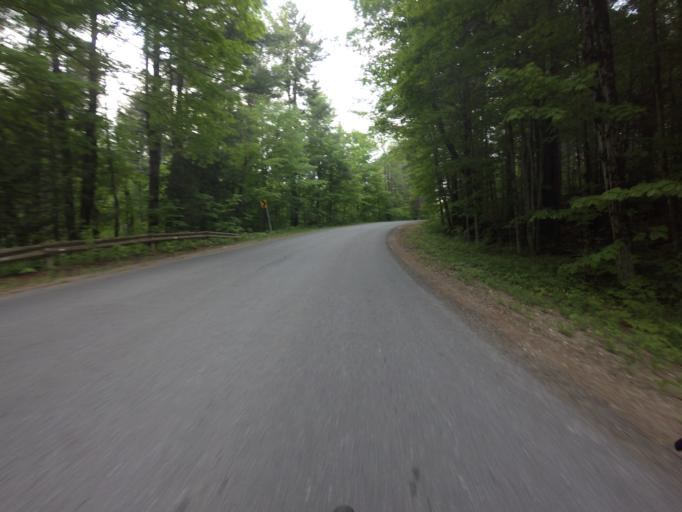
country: US
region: New York
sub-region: St. Lawrence County
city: Gouverneur
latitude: 44.1473
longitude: -75.3546
